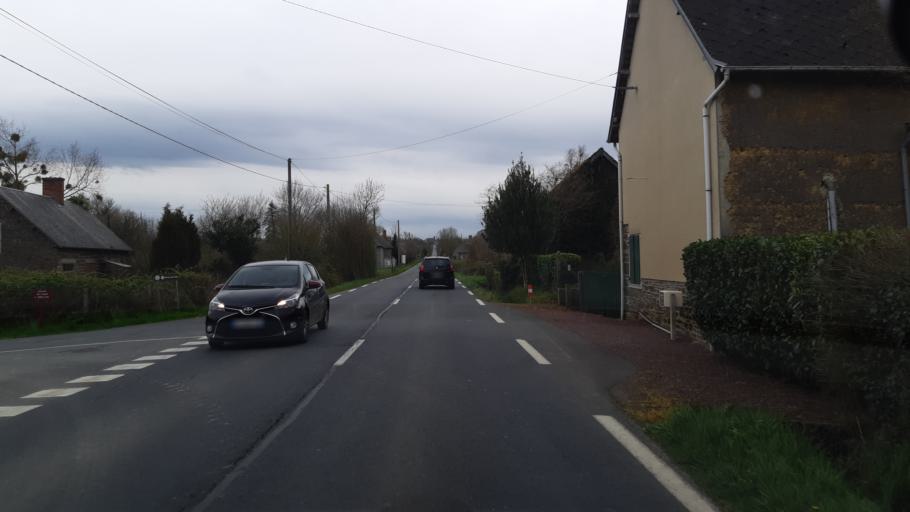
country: FR
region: Lower Normandy
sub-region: Departement de la Manche
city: Percy
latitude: 48.9788
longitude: -1.1607
